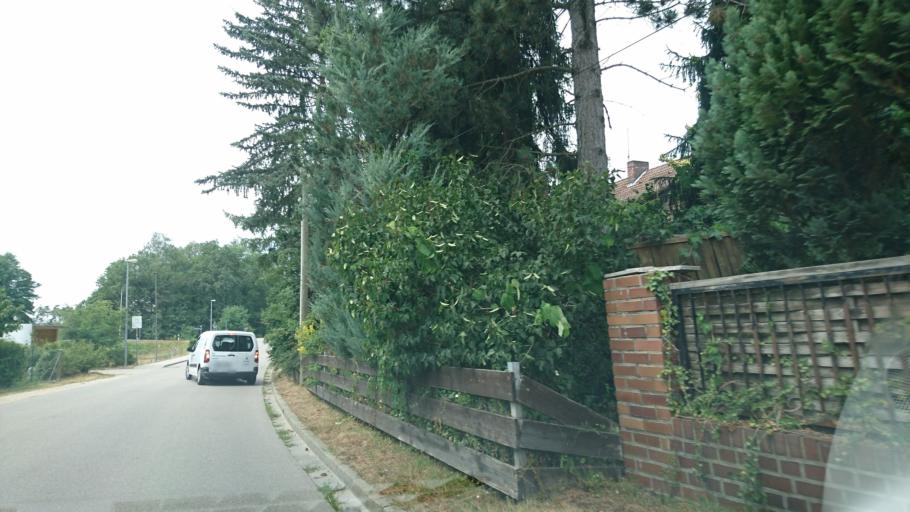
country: DE
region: Bavaria
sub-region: Regierungsbezirk Mittelfranken
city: Roth
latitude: 49.2105
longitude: 11.0808
